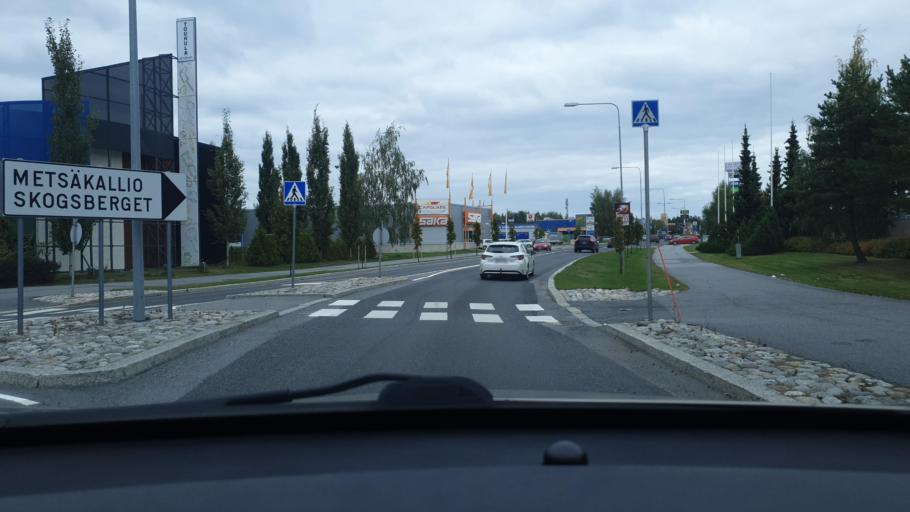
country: FI
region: Ostrobothnia
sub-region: Vaasa
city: Korsholm
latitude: 63.1087
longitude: 21.6491
